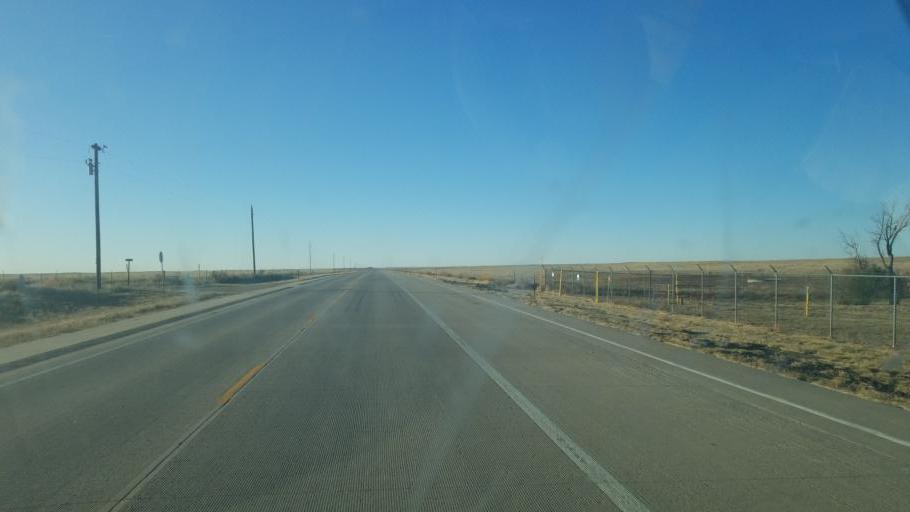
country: US
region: Colorado
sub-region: Kiowa County
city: Eads
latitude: 38.6589
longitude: -102.7859
